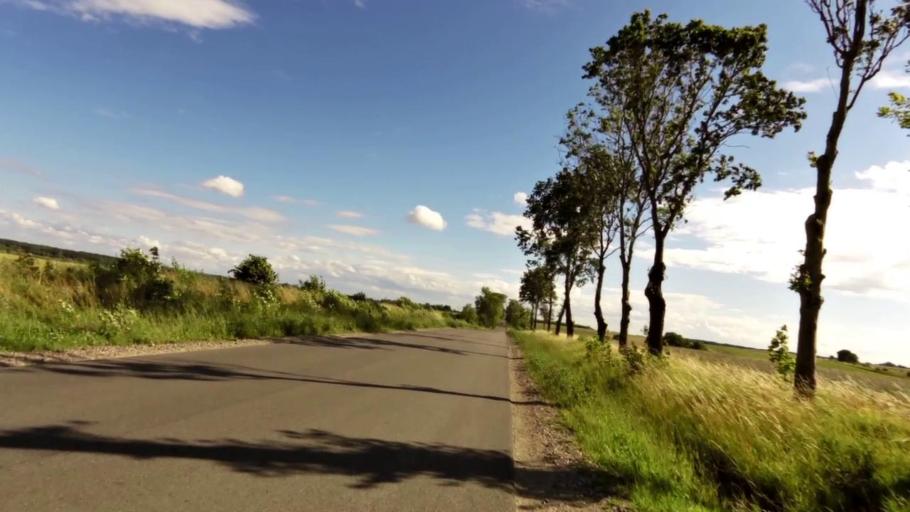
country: PL
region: West Pomeranian Voivodeship
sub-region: Powiat slawienski
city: Slawno
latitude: 54.4480
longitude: 16.7367
